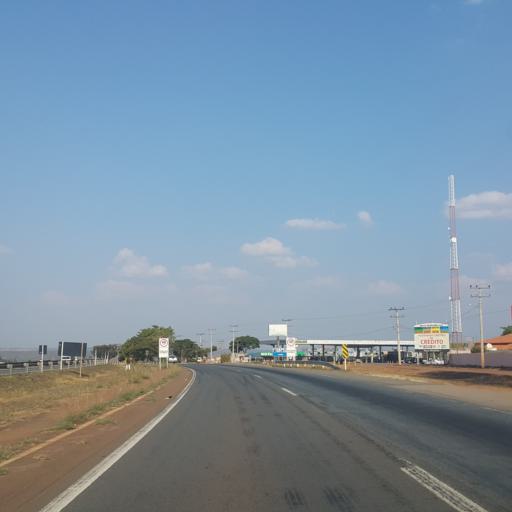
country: BR
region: Goias
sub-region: Abadiania
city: Abadiania
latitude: -16.1204
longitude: -48.4280
